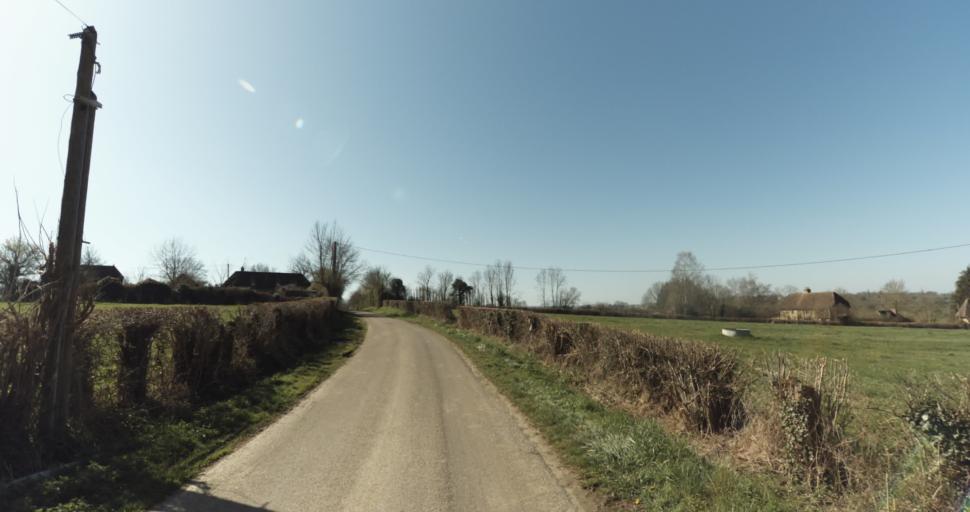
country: FR
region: Lower Normandy
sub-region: Departement du Calvados
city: Saint-Pierre-sur-Dives
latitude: 48.9743
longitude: 0.0527
